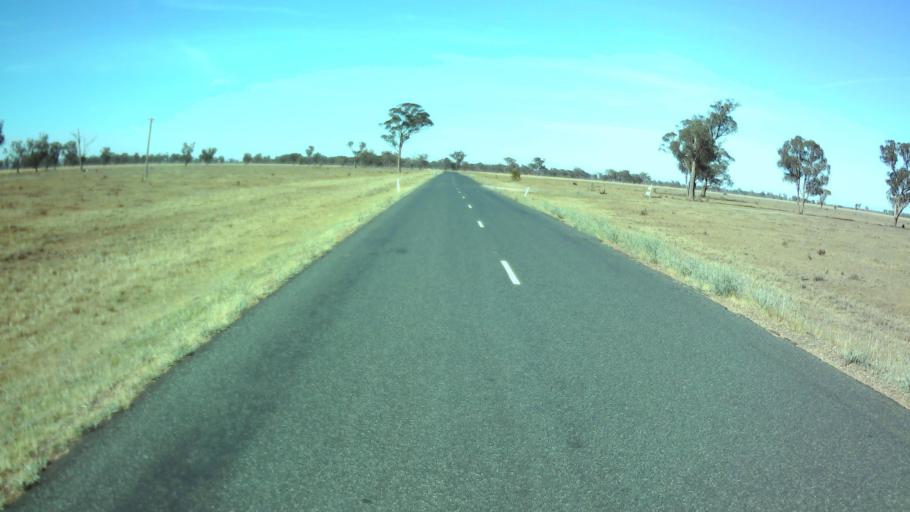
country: AU
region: New South Wales
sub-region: Weddin
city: Grenfell
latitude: -34.0477
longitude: 147.9222
